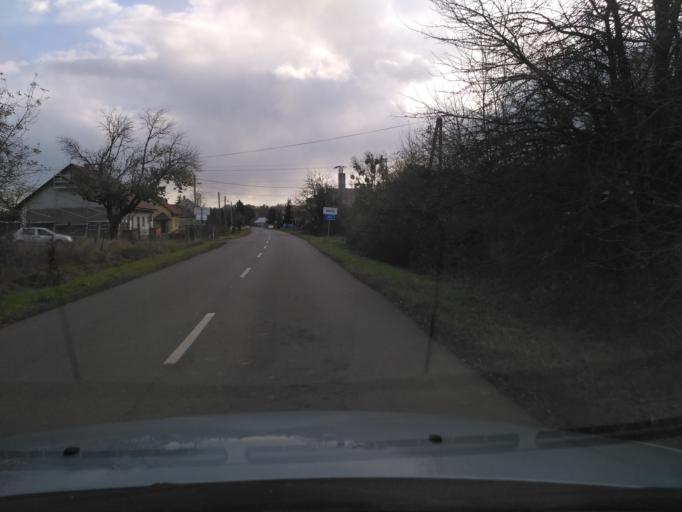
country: HU
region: Borsod-Abauj-Zemplen
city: Satoraljaujhely
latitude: 48.3990
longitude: 21.7095
